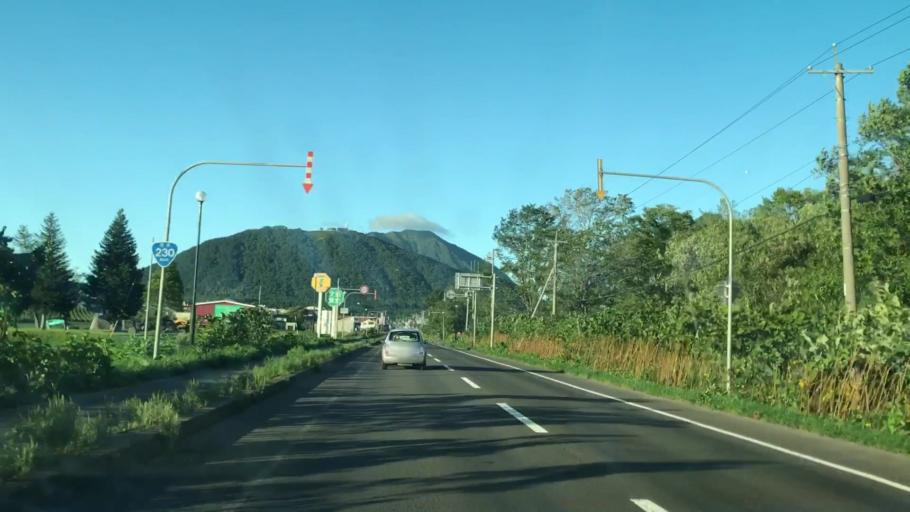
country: JP
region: Hokkaido
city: Niseko Town
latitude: 42.7295
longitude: 140.8696
